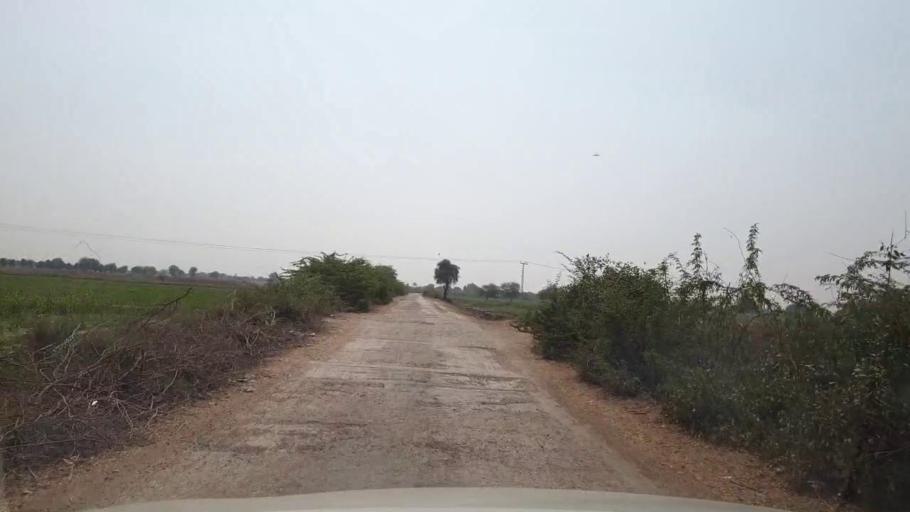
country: PK
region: Sindh
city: Dhoro Naro
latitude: 25.4727
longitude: 69.6382
